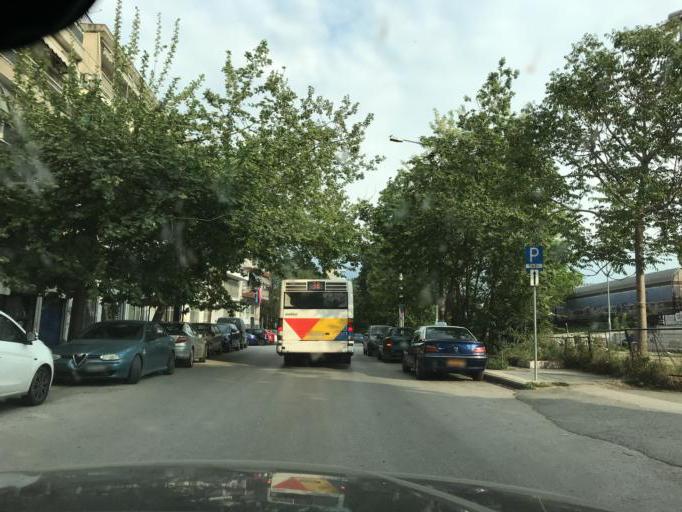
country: GR
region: Central Macedonia
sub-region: Nomos Thessalonikis
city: Thessaloniki
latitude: 40.6457
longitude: 22.9294
